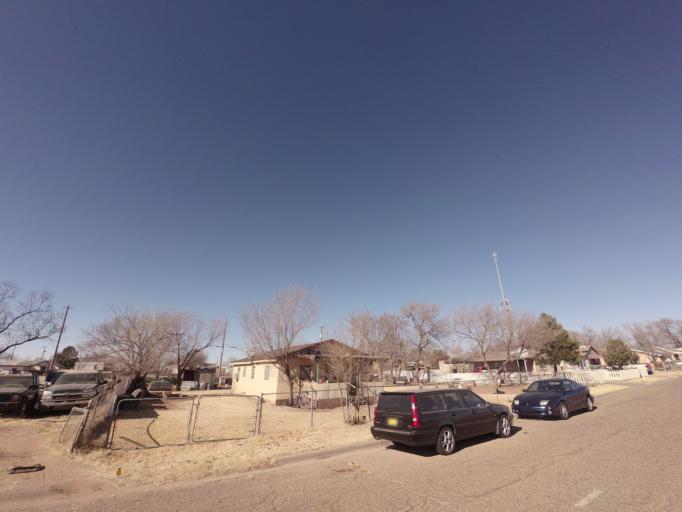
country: US
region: New Mexico
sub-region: Curry County
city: Clovis
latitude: 34.4016
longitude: -103.2322
